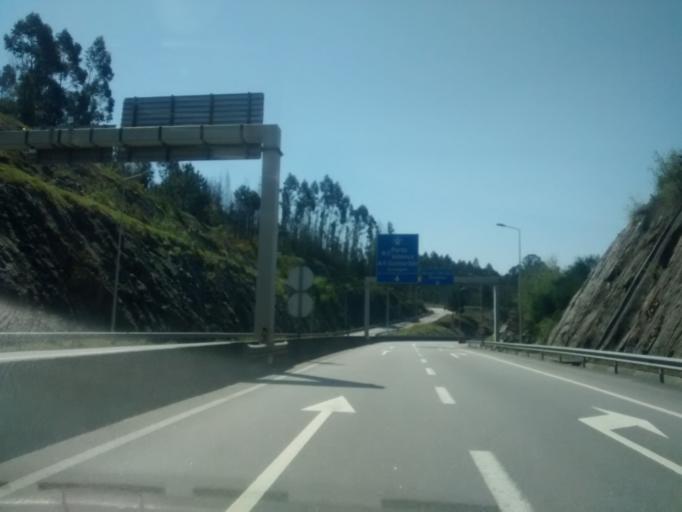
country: PT
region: Braga
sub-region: Braga
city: Braga
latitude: 41.5173
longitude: -8.4428
